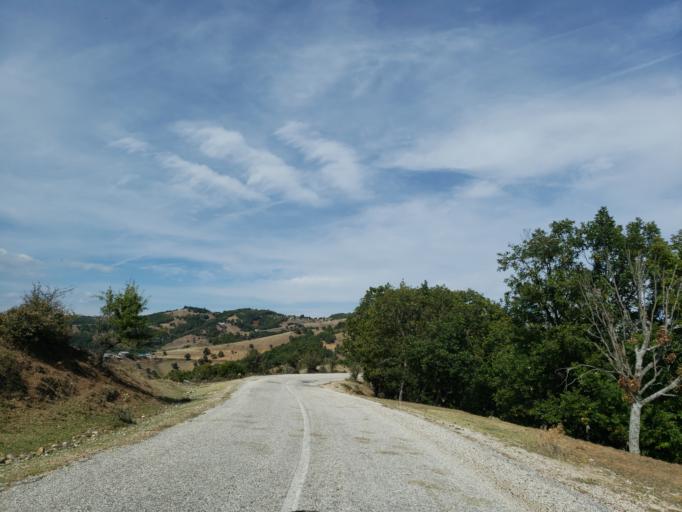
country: GR
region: Thessaly
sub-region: Trikala
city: Kastraki
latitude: 39.7542
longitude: 21.6613
